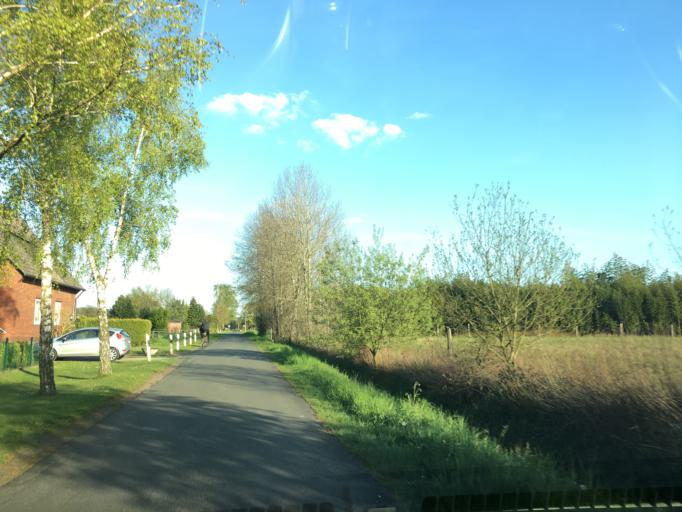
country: DE
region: North Rhine-Westphalia
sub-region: Regierungsbezirk Munster
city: Greven
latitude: 52.0481
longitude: 7.5924
